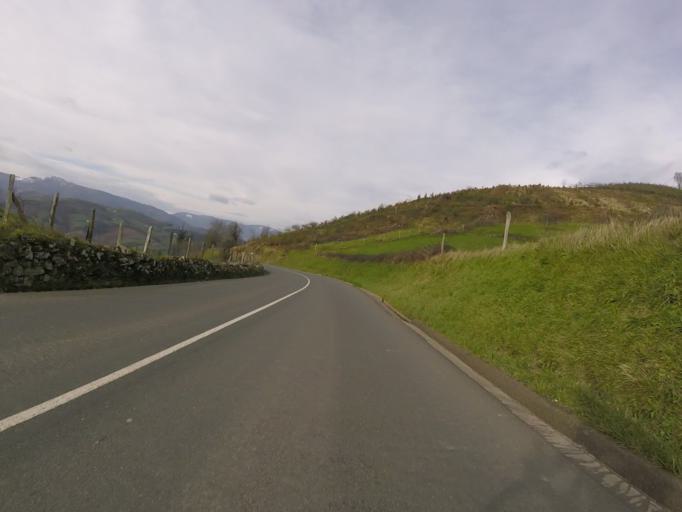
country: ES
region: Basque Country
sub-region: Provincia de Guipuzcoa
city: Azpeitia
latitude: 43.1692
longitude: -2.2313
